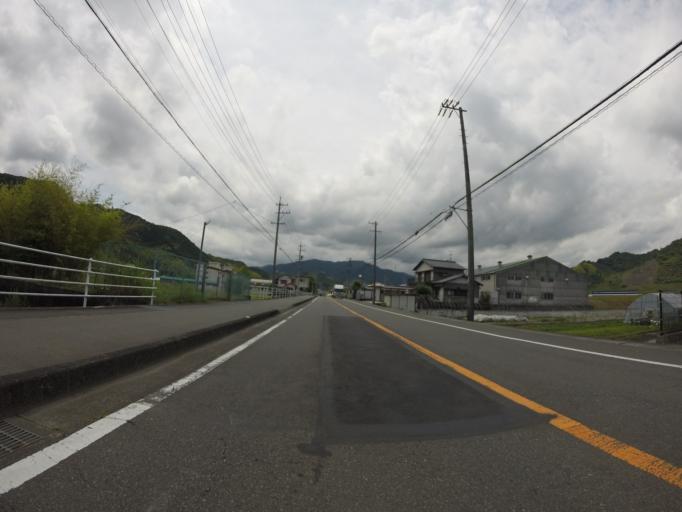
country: JP
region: Shizuoka
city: Shizuoka-shi
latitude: 34.9797
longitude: 138.3182
